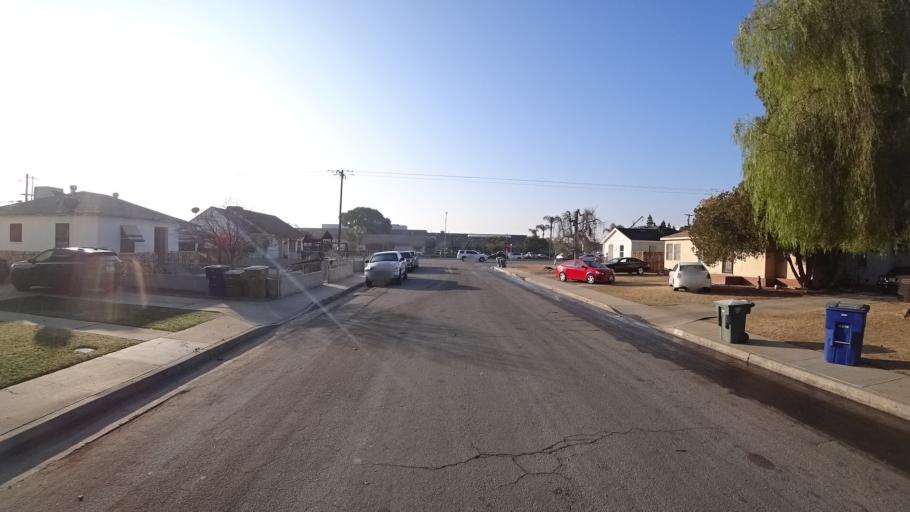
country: US
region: California
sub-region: Kern County
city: Bakersfield
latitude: 35.3547
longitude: -119.0425
